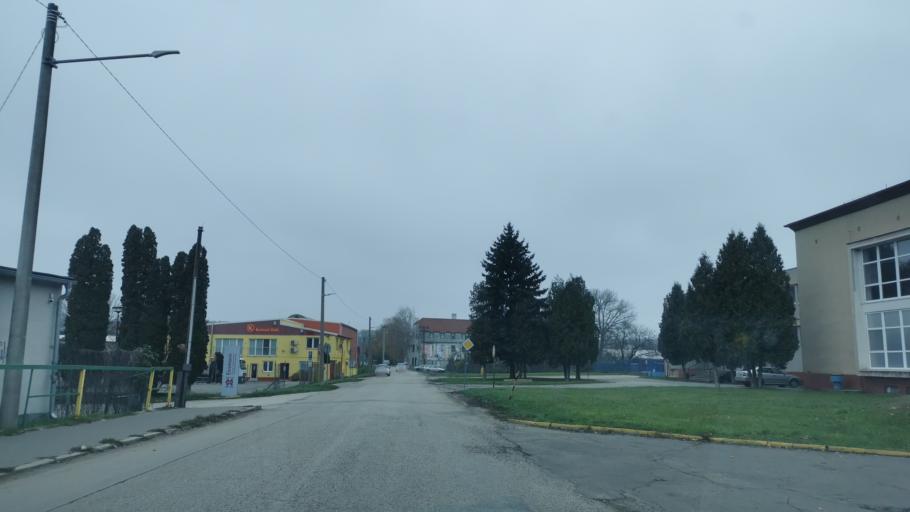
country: SK
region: Trnavsky
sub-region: Okres Skalica
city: Holic
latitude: 48.8218
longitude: 17.1572
